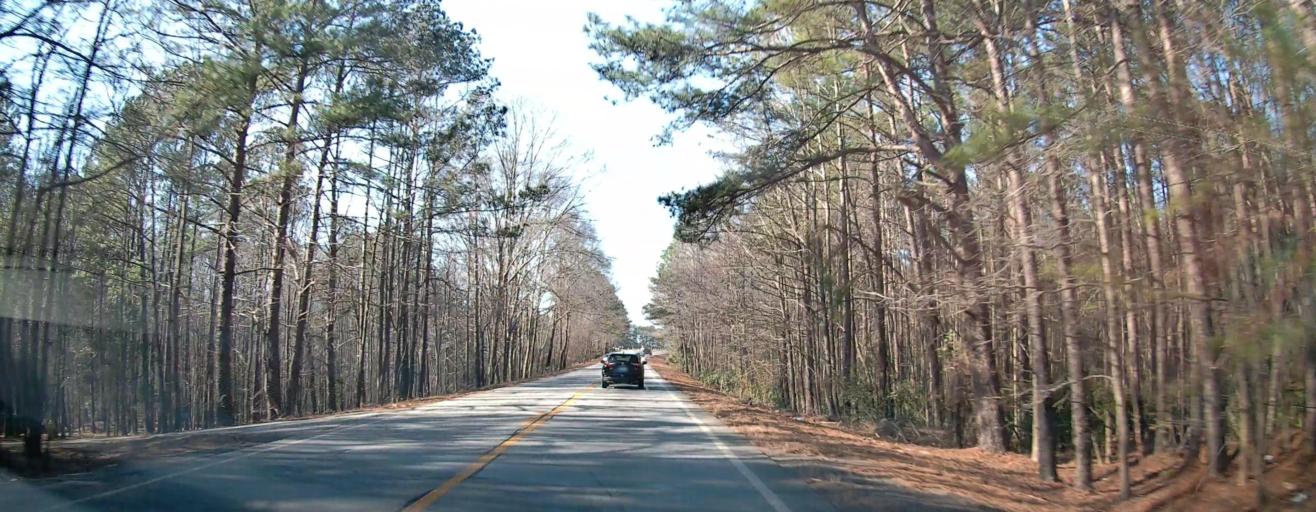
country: US
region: Georgia
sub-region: Butts County
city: Indian Springs
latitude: 33.2609
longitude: -83.9048
